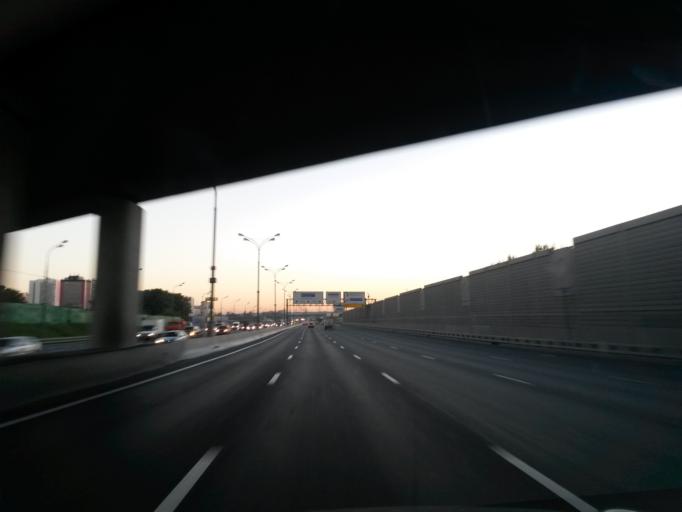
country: RU
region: Moscow
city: Vostochnyy
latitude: 55.8072
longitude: 37.8397
